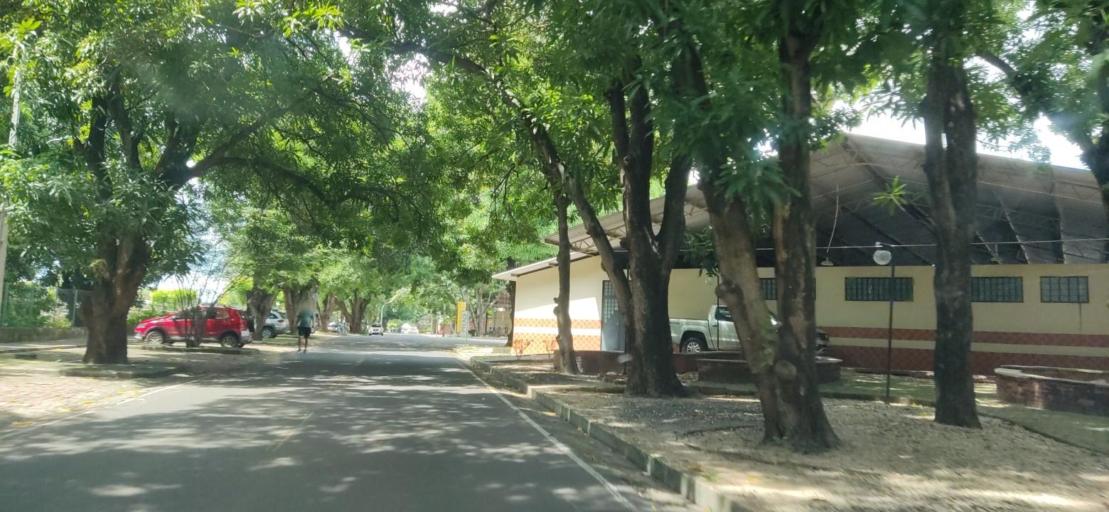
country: BR
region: Piaui
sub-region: Teresina
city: Teresina
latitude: -5.0575
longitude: -42.7923
